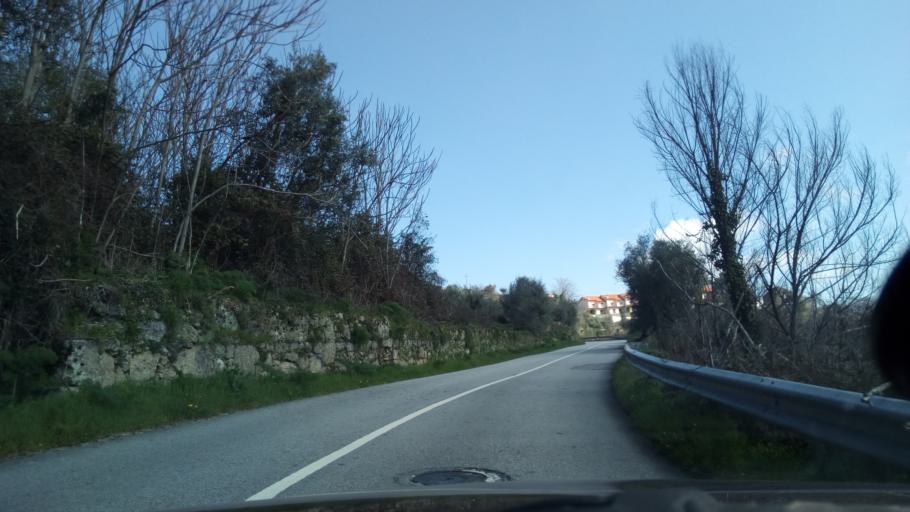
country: PT
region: Guarda
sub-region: Fornos de Algodres
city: Fornos de Algodres
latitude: 40.6283
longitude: -7.5377
